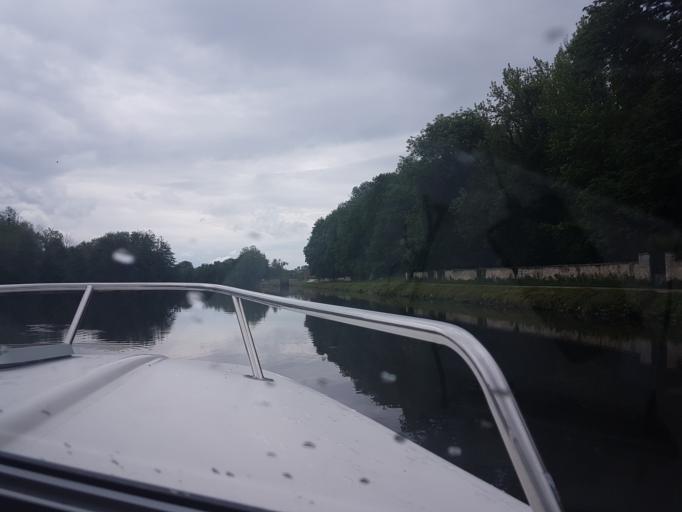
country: FR
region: Bourgogne
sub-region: Departement de l'Yonne
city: Saint-Bris-le-Vineux
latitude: 47.7001
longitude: 3.6389
